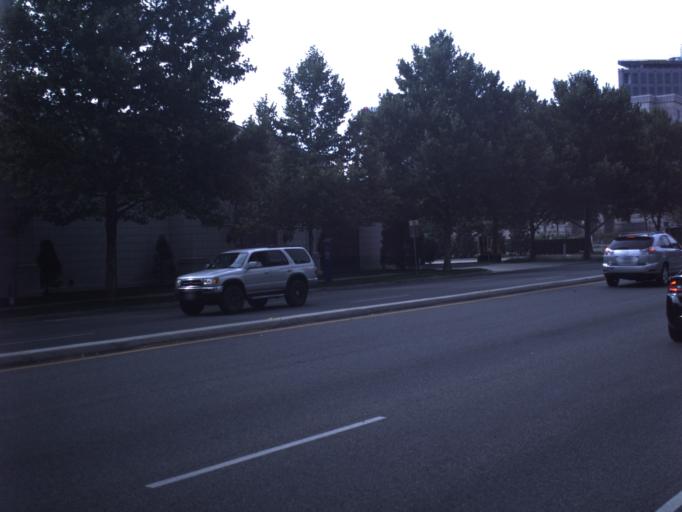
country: US
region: Utah
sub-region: Salt Lake County
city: Salt Lake City
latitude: 40.7574
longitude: -111.8881
